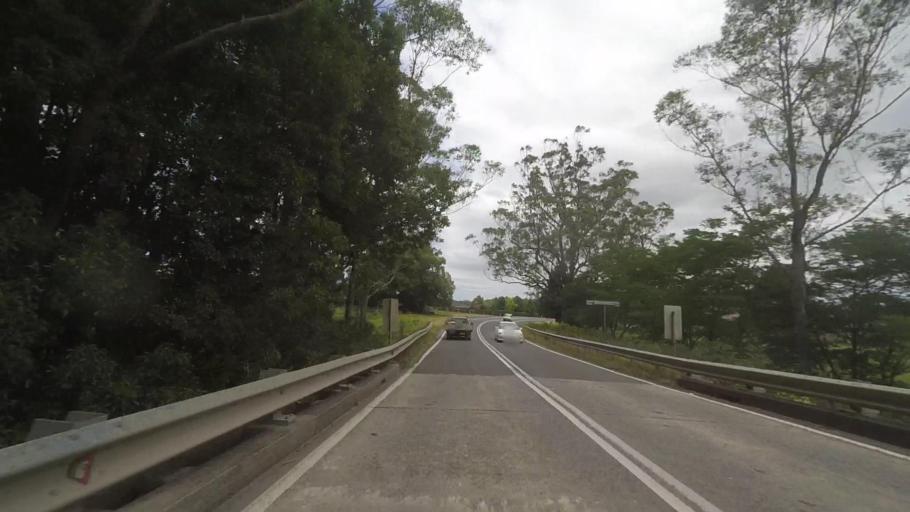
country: AU
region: New South Wales
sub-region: Shoalhaven Shire
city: Falls Creek
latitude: -35.0856
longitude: 150.5161
